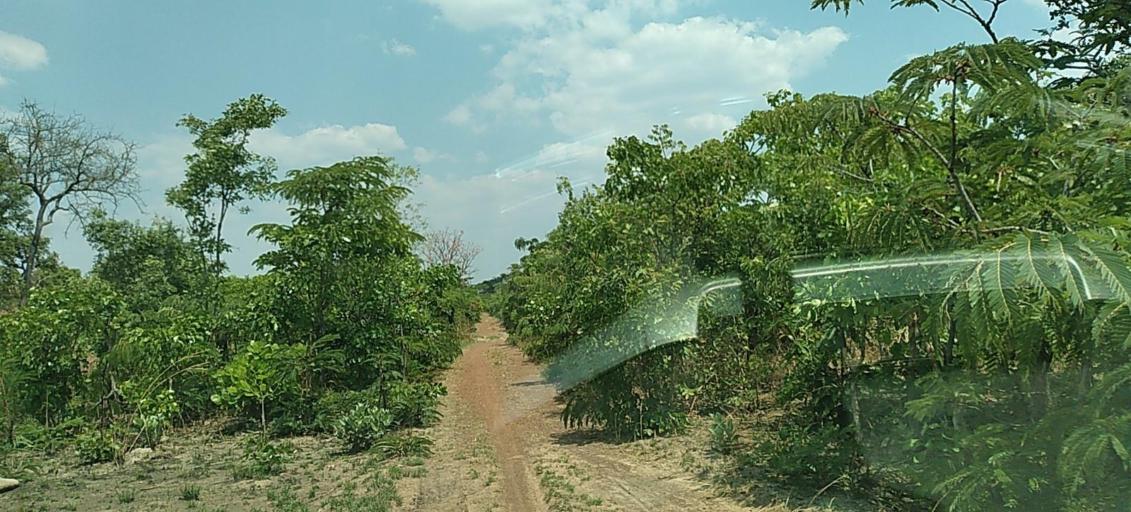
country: CD
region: Katanga
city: Kipushi
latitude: -12.0033
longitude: 27.4253
